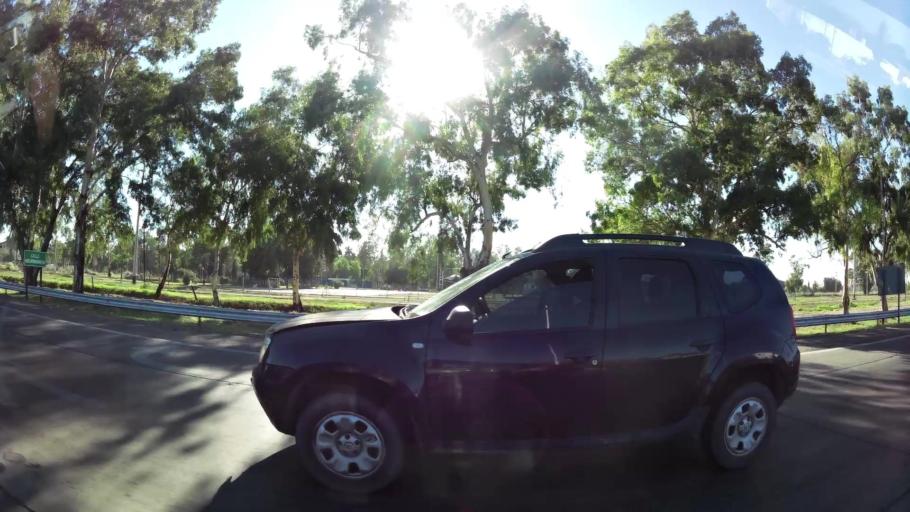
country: AR
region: Mendoza
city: Las Heras
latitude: -32.8431
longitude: -68.8024
